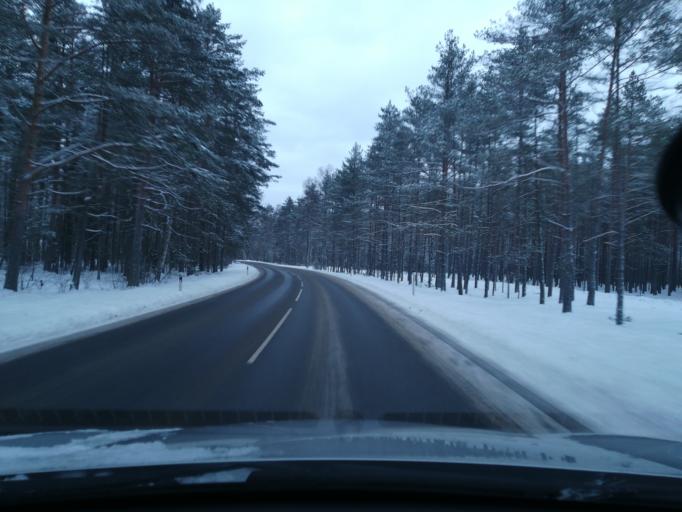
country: EE
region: Harju
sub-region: Paldiski linn
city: Paldiski
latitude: 59.3888
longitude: 24.2405
